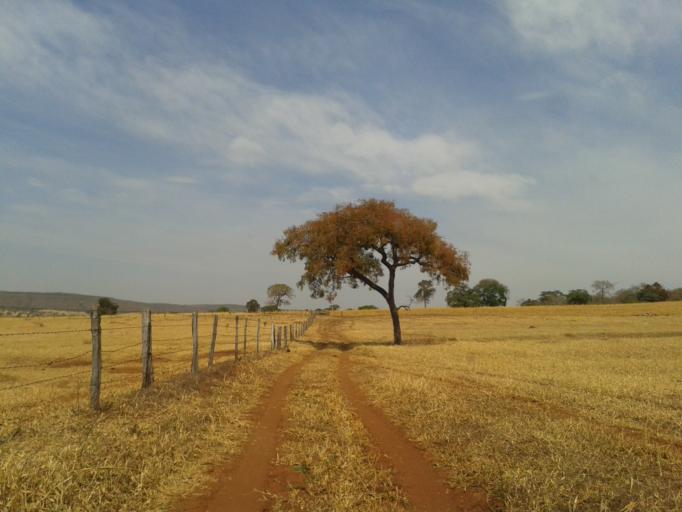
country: BR
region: Minas Gerais
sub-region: Santa Vitoria
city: Santa Vitoria
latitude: -19.2293
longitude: -50.0246
